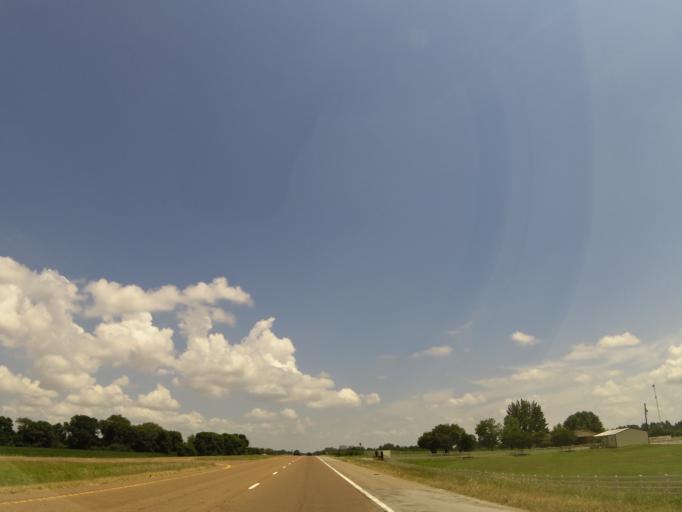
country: US
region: Tennessee
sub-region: Dyer County
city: Dyersburg
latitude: 35.9502
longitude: -89.3117
